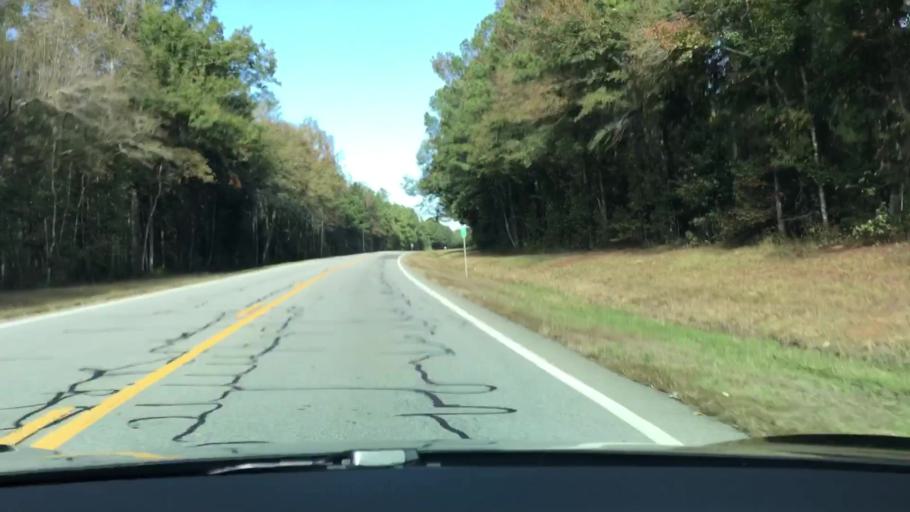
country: US
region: Georgia
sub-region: Warren County
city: Warrenton
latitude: 33.3476
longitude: -82.5828
